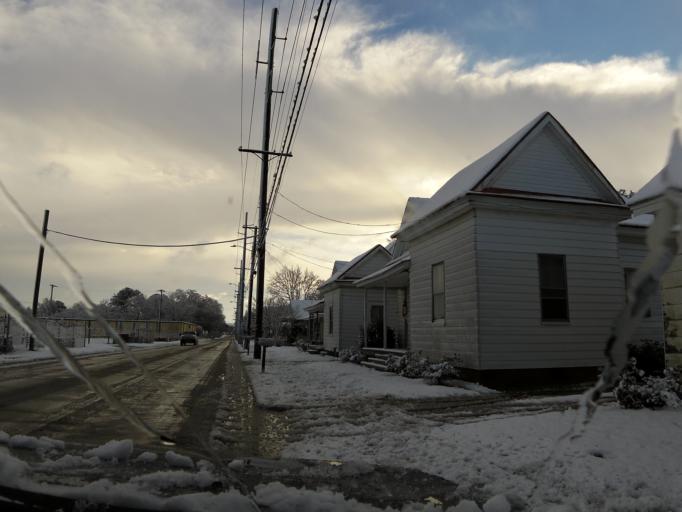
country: US
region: North Carolina
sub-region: Nash County
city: Rocky Mount
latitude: 35.9267
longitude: -77.8098
